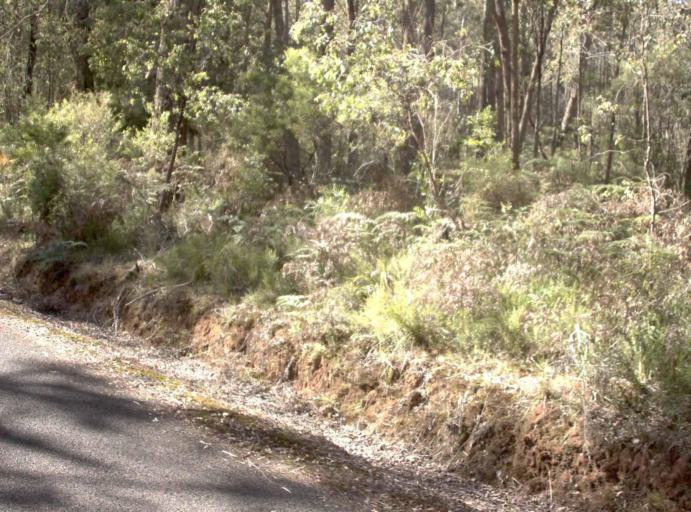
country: AU
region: New South Wales
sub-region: Bombala
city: Bombala
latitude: -37.3867
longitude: 148.6027
